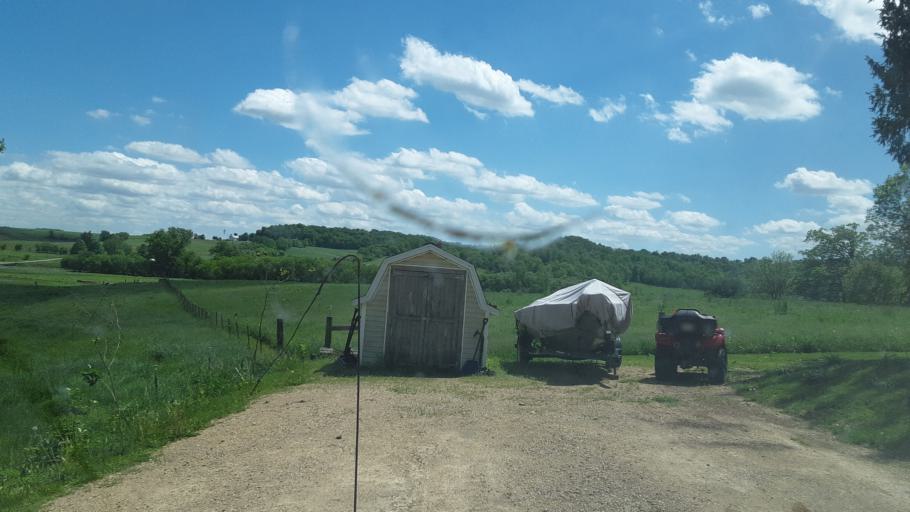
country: US
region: Wisconsin
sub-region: Vernon County
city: Hillsboro
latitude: 43.5257
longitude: -90.2205
